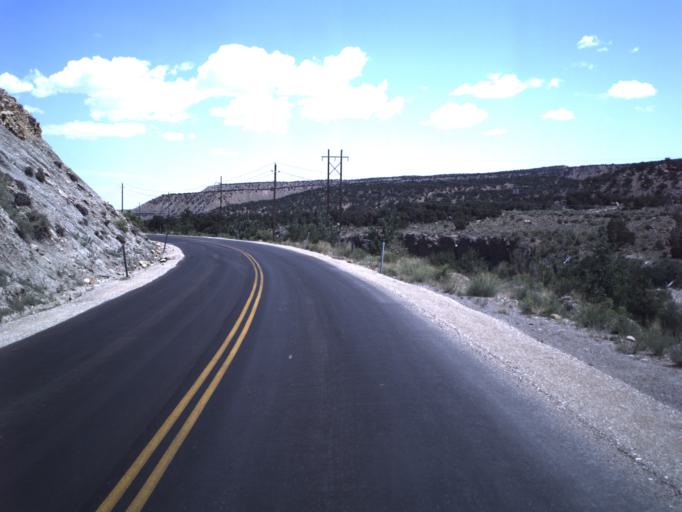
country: US
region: Utah
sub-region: Emery County
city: Orangeville
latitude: 39.2708
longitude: -111.1557
